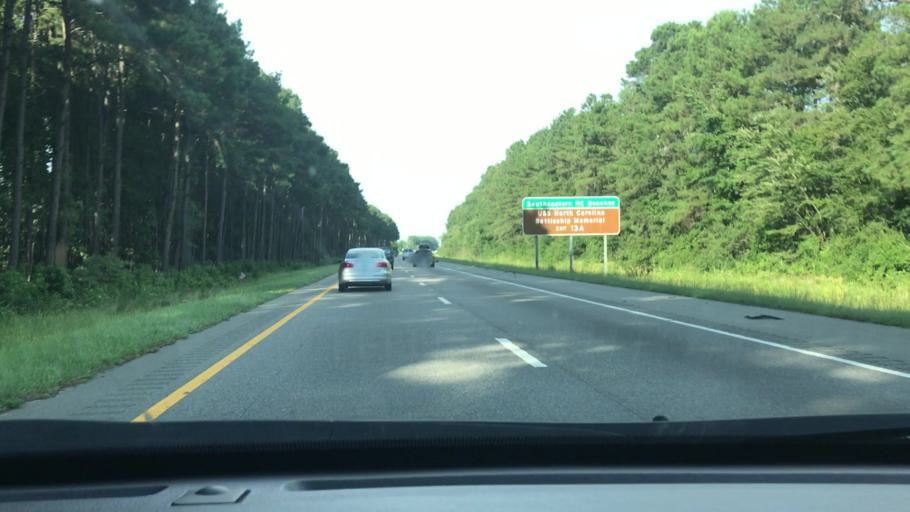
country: US
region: North Carolina
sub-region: Robeson County
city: Fairmont
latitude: 34.5821
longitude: -79.1405
